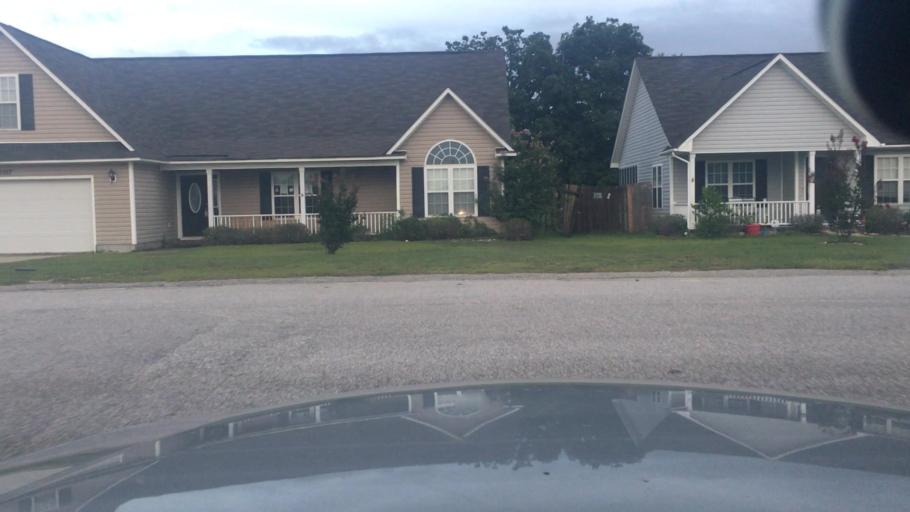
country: US
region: North Carolina
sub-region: Cumberland County
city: Hope Mills
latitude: 34.9861
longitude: -78.9126
